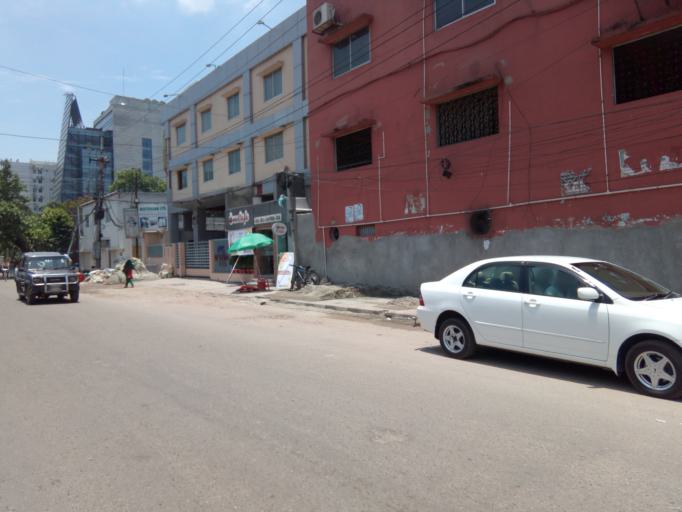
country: BD
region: Dhaka
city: Paltan
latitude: 23.7635
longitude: 90.4012
